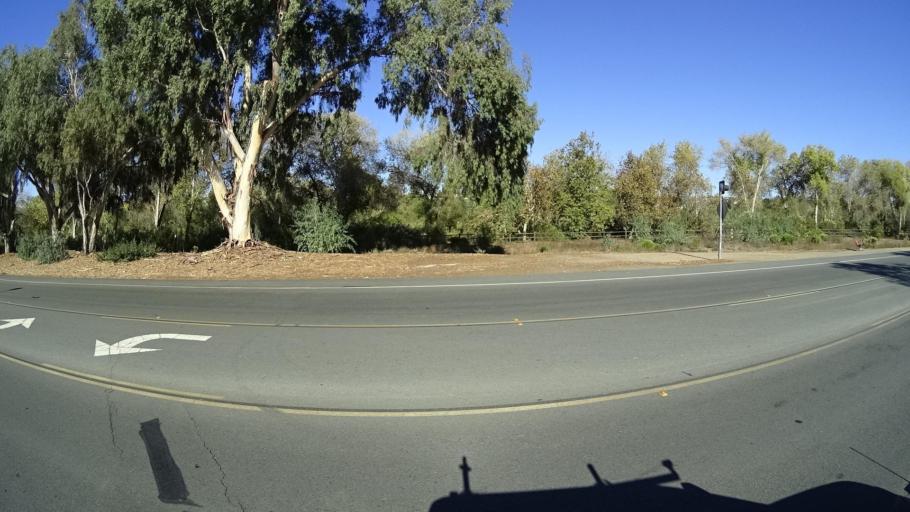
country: US
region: California
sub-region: San Diego County
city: Bonita
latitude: 32.6699
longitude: -117.0224
